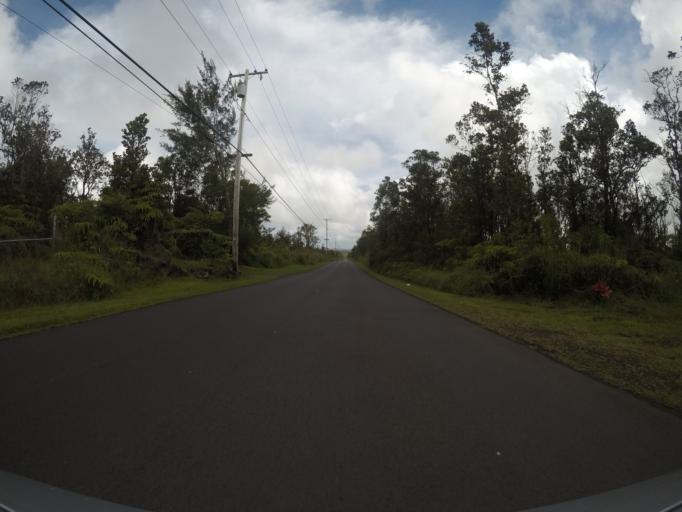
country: US
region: Hawaii
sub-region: Hawaii County
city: Fern Acres
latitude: 19.4711
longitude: -155.1377
